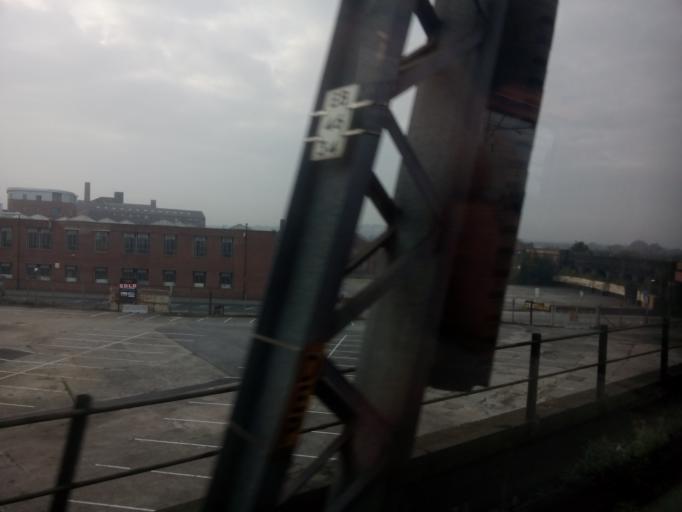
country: GB
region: England
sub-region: City and Borough of Leeds
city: Leeds
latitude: 53.7930
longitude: -1.5544
